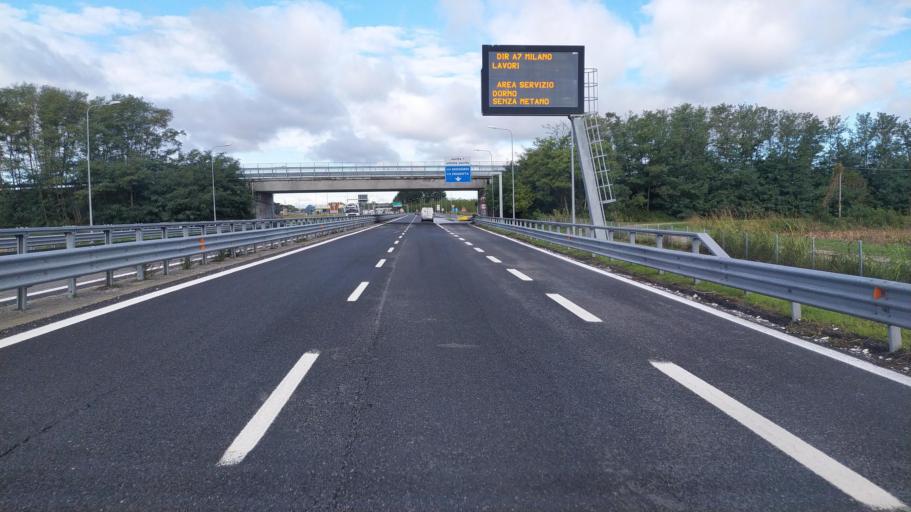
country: IT
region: Lombardy
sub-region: Provincia di Pavia
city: Trivolzio
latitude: 45.2438
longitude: 9.0549
